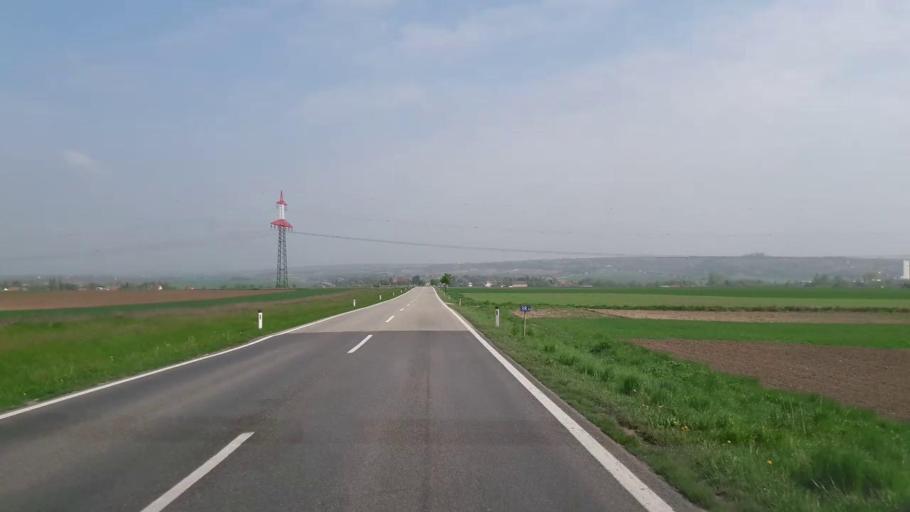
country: AT
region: Lower Austria
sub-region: Politischer Bezirk Hollabrunn
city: Haugsdorf
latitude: 48.6941
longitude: 16.0579
